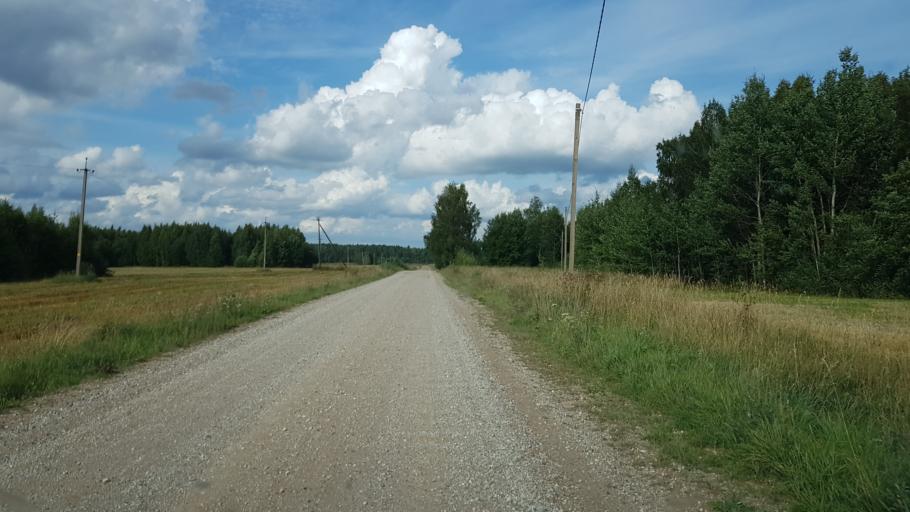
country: RU
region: Pskov
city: Pechory
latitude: 57.8062
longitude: 27.5083
